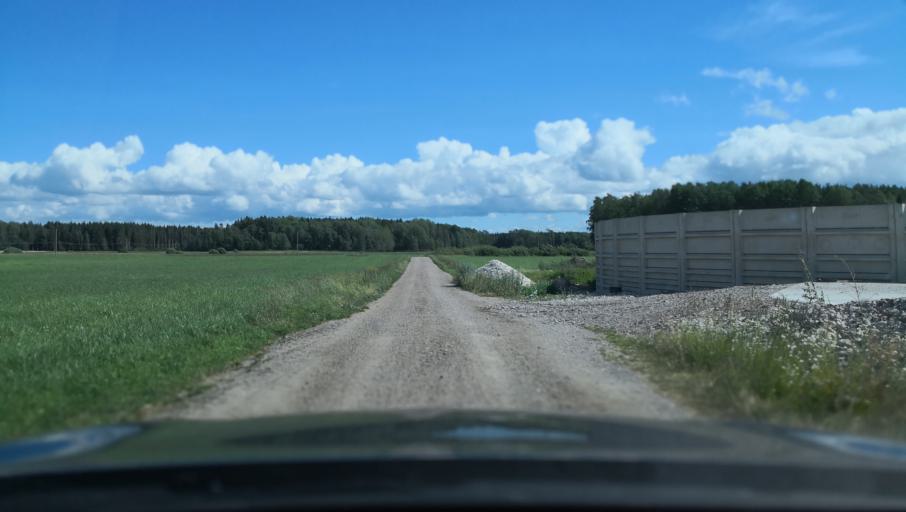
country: SE
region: Vaestmanland
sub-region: Kungsors Kommun
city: Kungsoer
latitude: 59.3208
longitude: 16.0627
